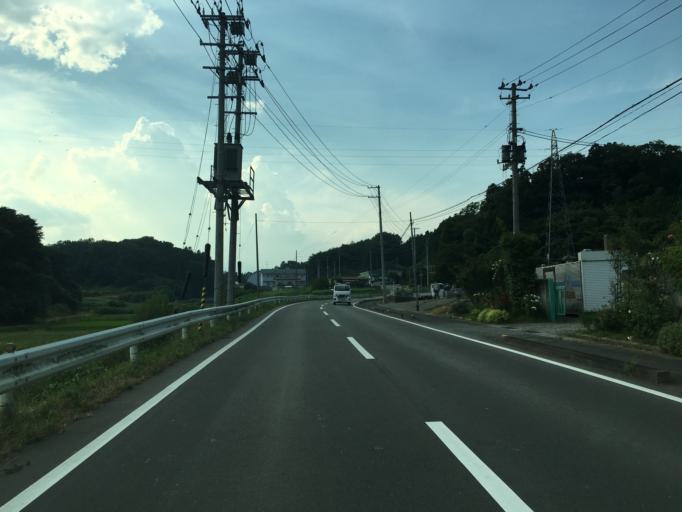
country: JP
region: Fukushima
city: Nihommatsu
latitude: 37.5709
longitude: 140.4345
